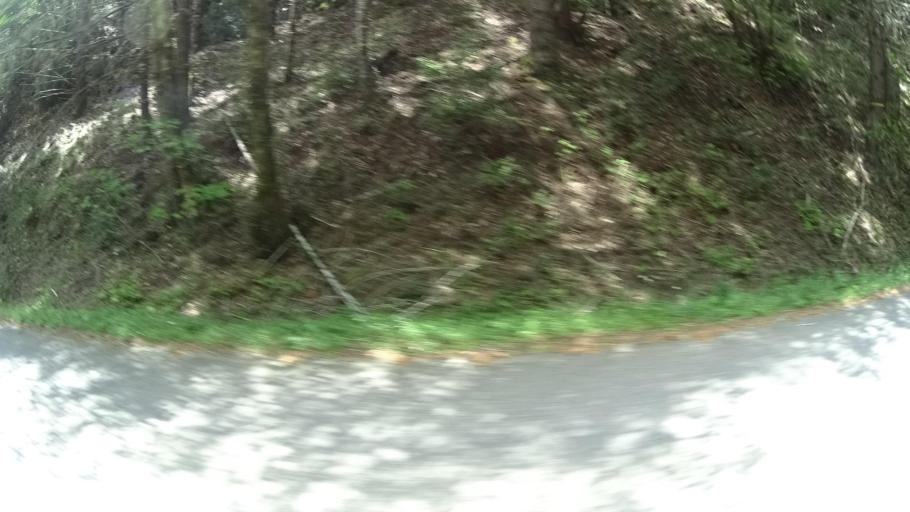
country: US
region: California
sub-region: Humboldt County
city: Redway
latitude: 40.0815
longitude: -123.9521
